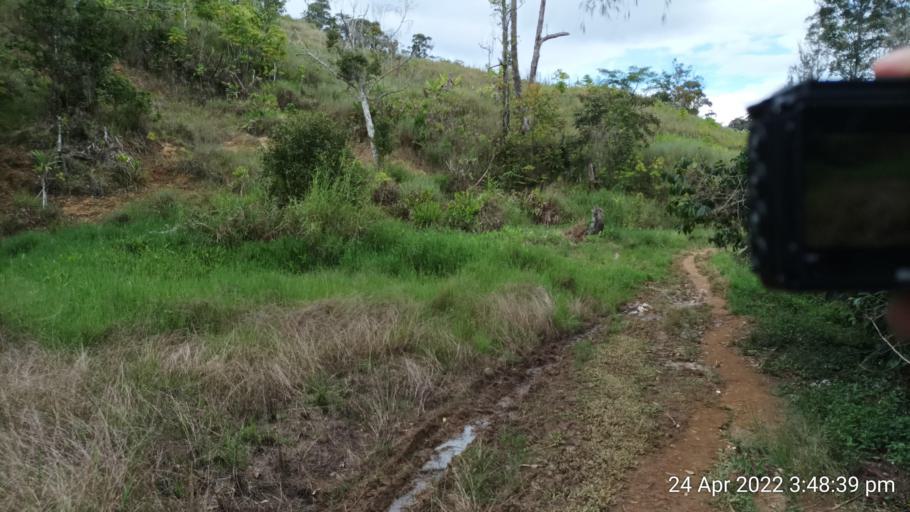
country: PG
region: Jiwaka
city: Minj
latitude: -5.8965
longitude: 144.8232
